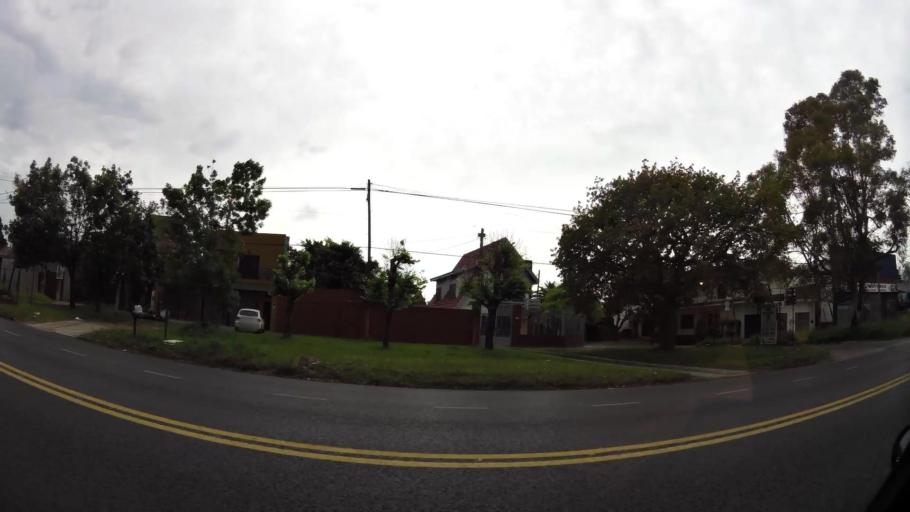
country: AR
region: Buenos Aires
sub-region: Partido de Quilmes
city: Quilmes
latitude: -34.7605
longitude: -58.2869
